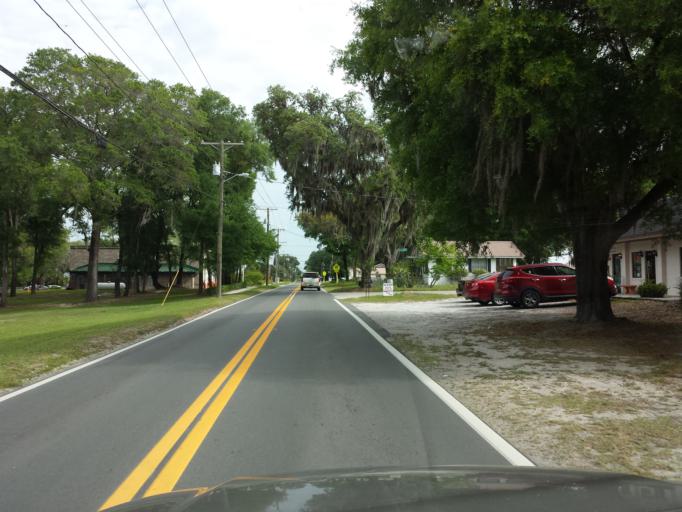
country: US
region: Florida
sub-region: Pasco County
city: San Antonio
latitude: 28.3346
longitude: -82.2743
